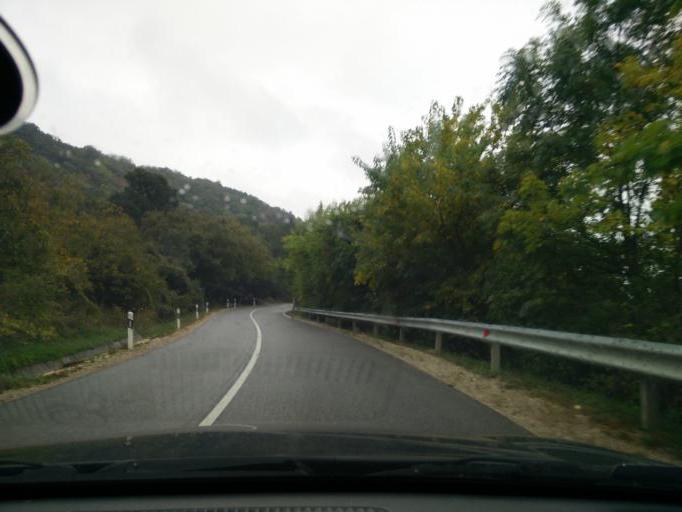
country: HU
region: Komarom-Esztergom
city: Tarjan
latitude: 47.6414
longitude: 18.5403
